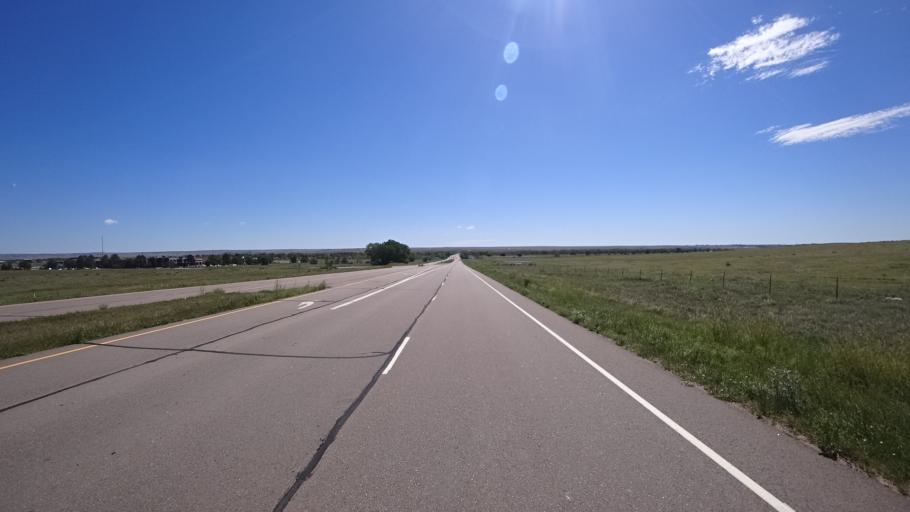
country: US
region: Colorado
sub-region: El Paso County
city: Security-Widefield
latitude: 38.7622
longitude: -104.6716
